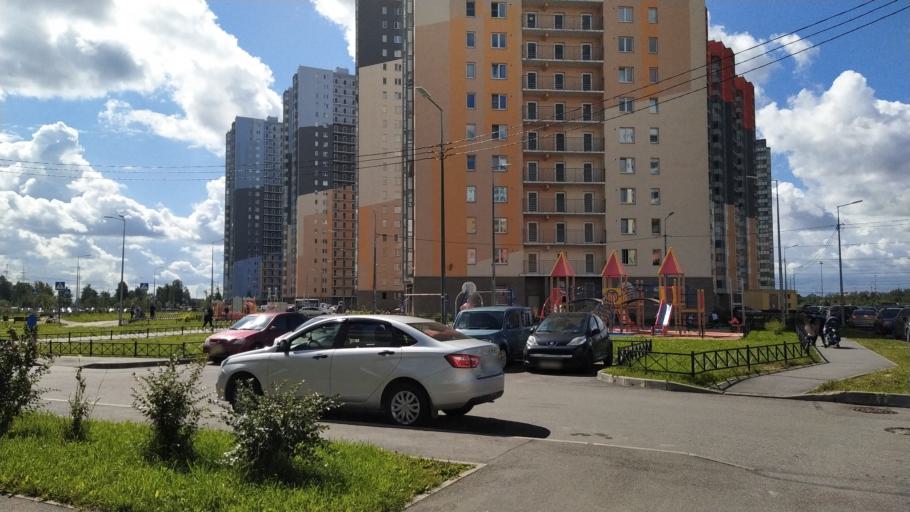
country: RU
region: Leningrad
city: Murino
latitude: 60.0297
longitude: 30.4565
